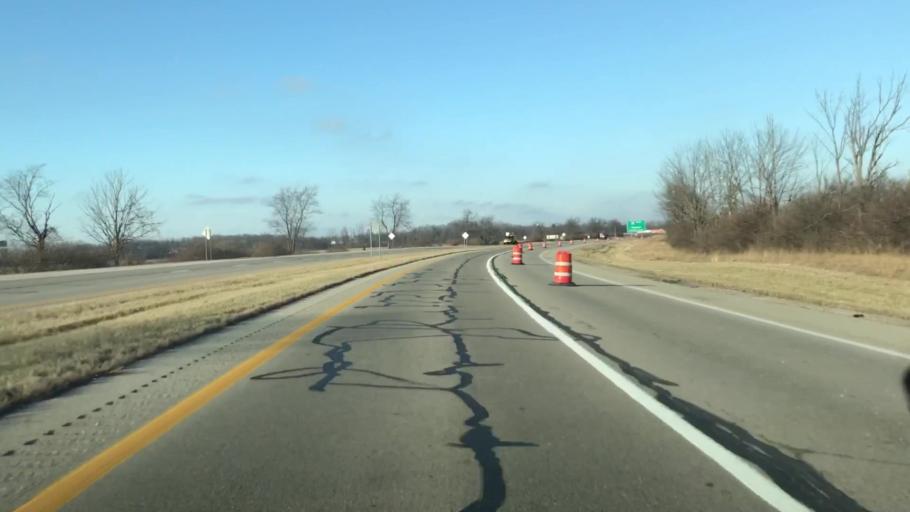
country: US
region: Ohio
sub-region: Clark County
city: Springfield
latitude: 39.8848
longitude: -83.8540
